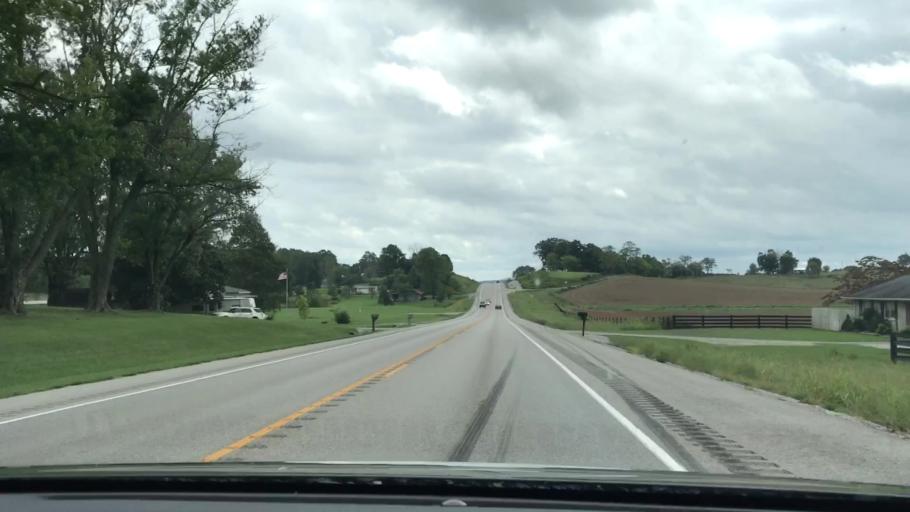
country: US
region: Kentucky
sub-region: Barren County
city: Glasgow
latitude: 36.9524
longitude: -85.8520
